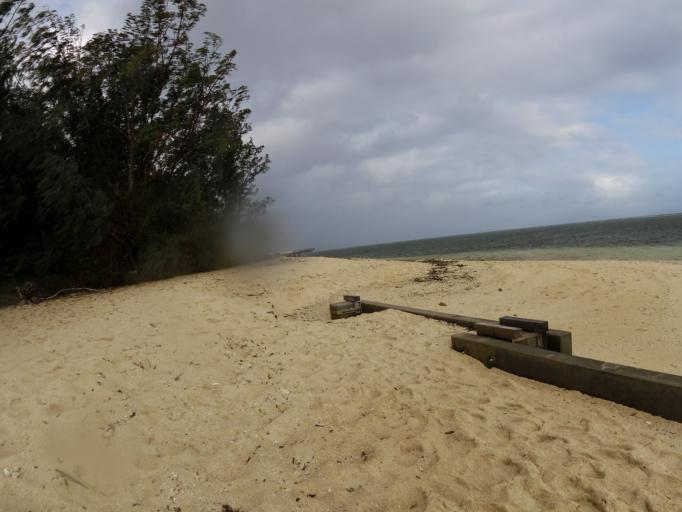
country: AU
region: Queensland
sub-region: Cairns
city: Yorkeys Knob
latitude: -16.7598
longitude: 145.9711
